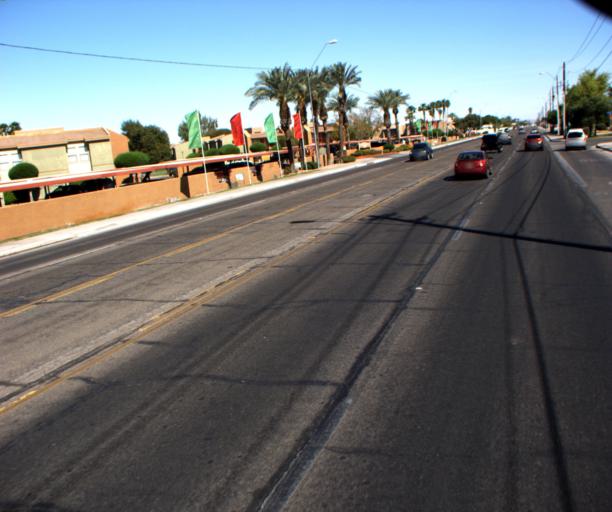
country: US
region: Arizona
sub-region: Yuma County
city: Yuma
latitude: 32.6850
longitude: -114.6503
